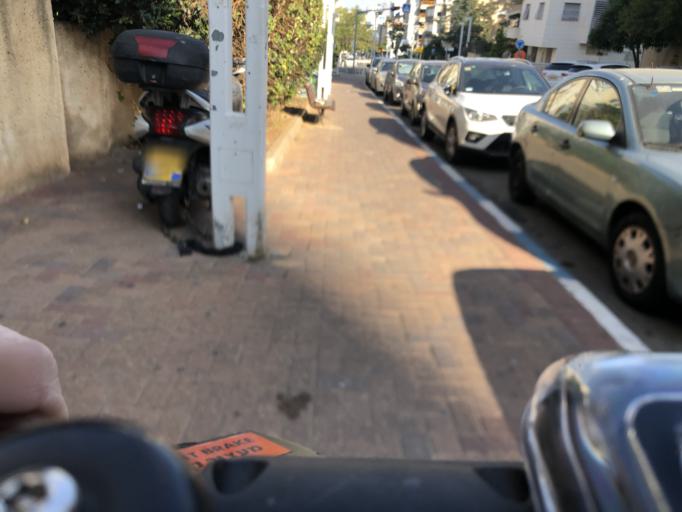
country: IL
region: Tel Aviv
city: Giv`atayim
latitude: 32.0677
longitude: 34.8124
